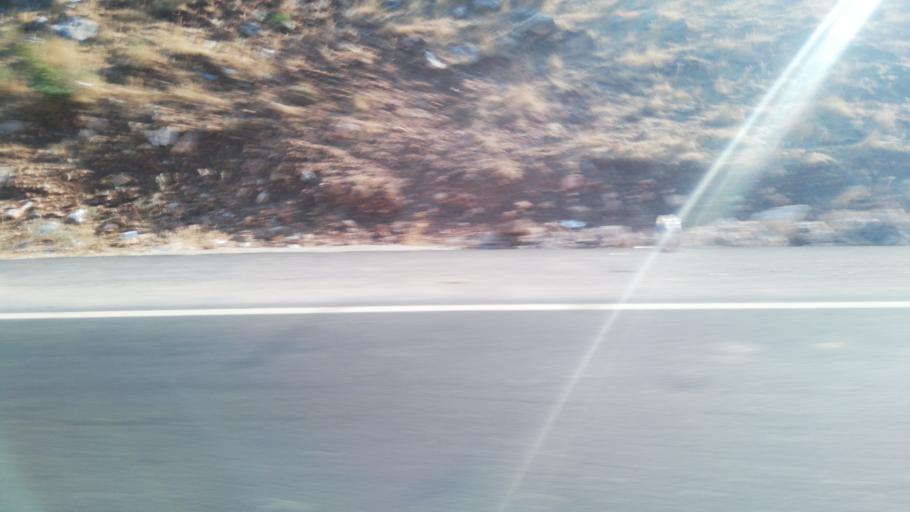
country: TR
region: Mardin
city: Sivrice
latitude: 37.2278
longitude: 41.3296
